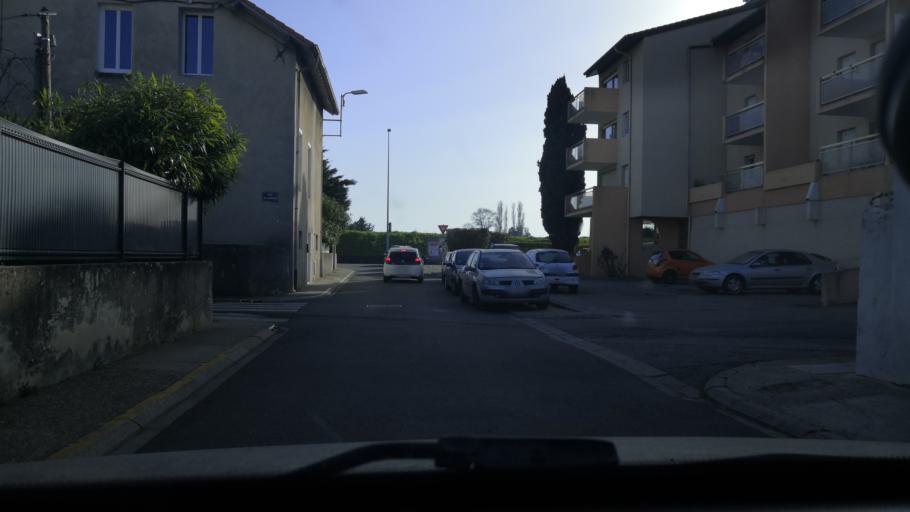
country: FR
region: Rhone-Alpes
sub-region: Departement de la Drome
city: Montelimar
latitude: 44.5547
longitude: 4.7407
